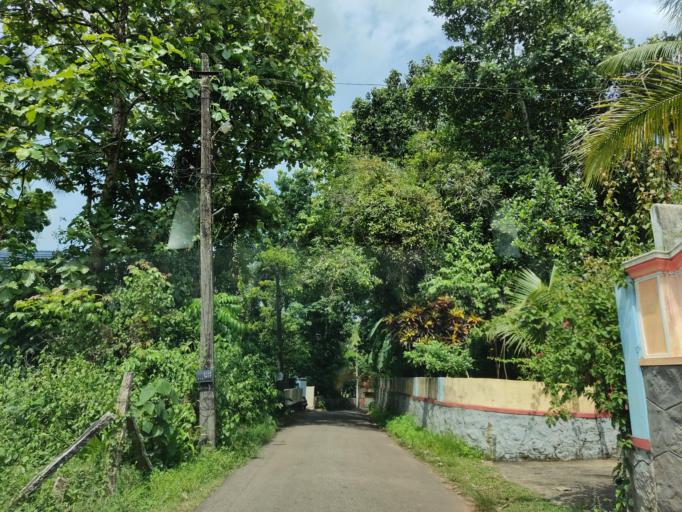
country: IN
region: Kerala
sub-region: Alappuzha
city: Mavelikara
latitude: 9.2581
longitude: 76.5657
